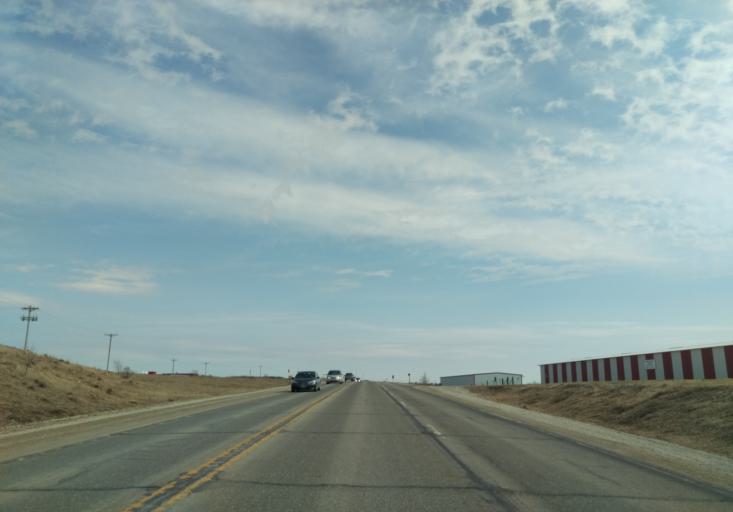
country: US
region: Iowa
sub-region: Winneshiek County
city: Decorah
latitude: 43.2758
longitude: -91.7355
